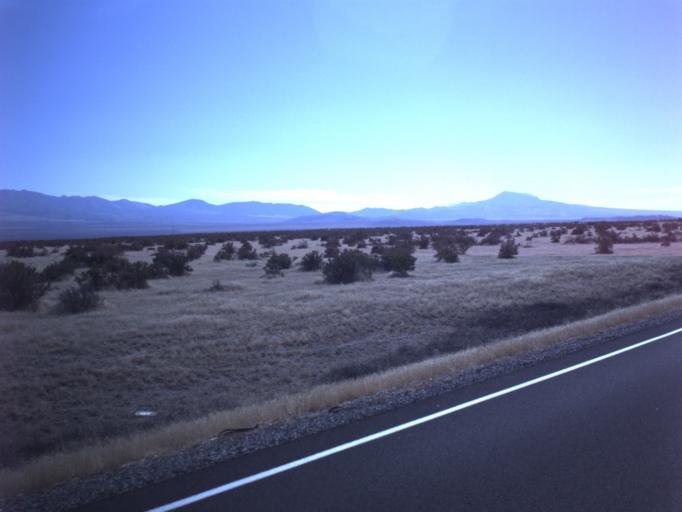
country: US
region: Utah
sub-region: Tooele County
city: Grantsville
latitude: 40.2800
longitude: -112.7418
